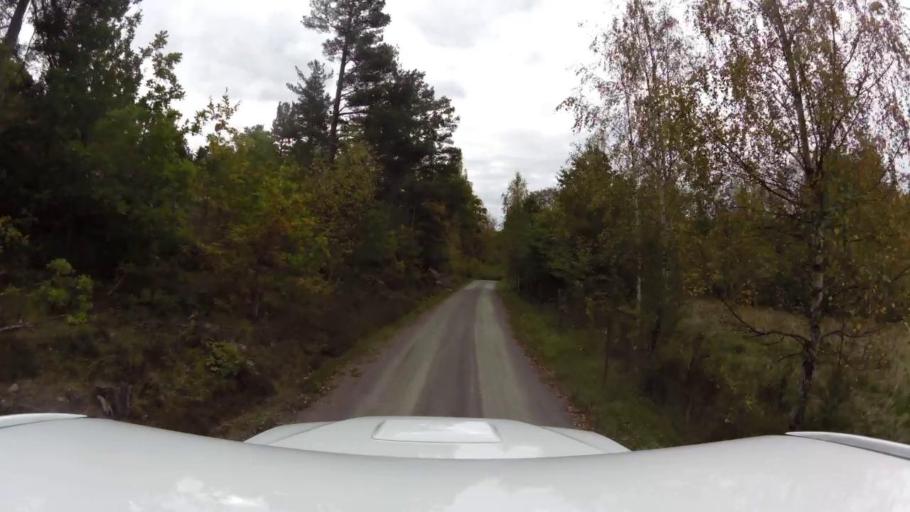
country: SE
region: OEstergoetland
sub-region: Kinda Kommun
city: Rimforsa
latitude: 58.2213
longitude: 15.6236
